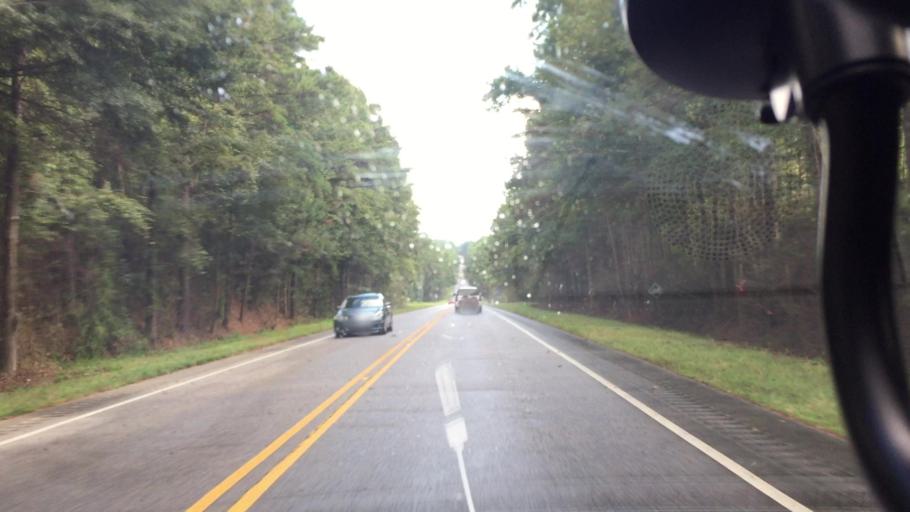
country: US
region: Alabama
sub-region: Coffee County
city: New Brockton
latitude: 31.4091
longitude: -85.8830
